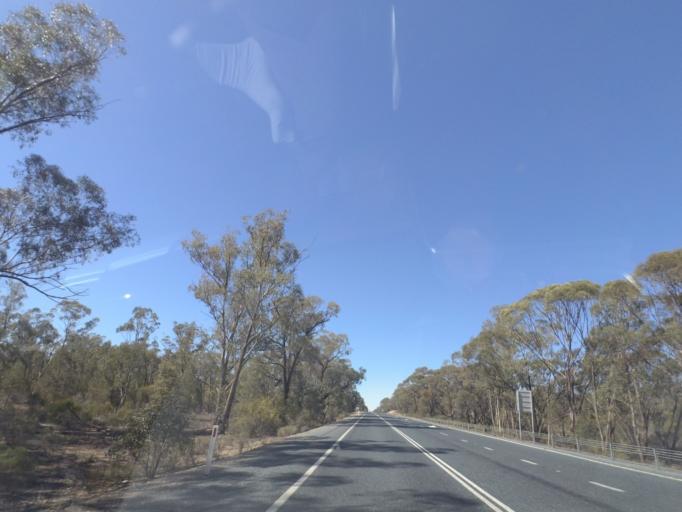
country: AU
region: New South Wales
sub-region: Bland
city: West Wyalong
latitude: -34.1259
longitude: 147.1255
